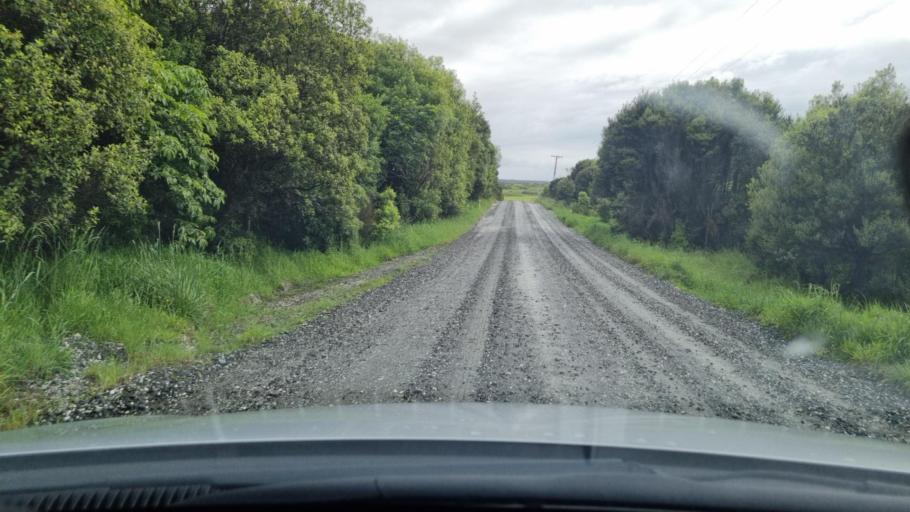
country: NZ
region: Southland
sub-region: Invercargill City
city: Bluff
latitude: -46.5244
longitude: 168.2708
